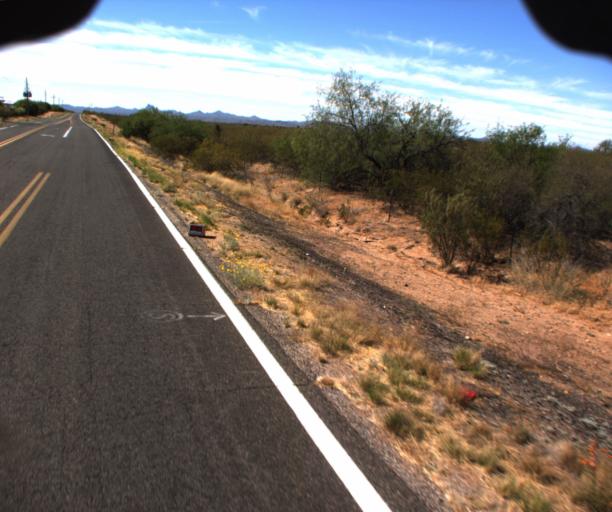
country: US
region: Arizona
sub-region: Yavapai County
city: Congress
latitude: 34.1058
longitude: -112.8318
